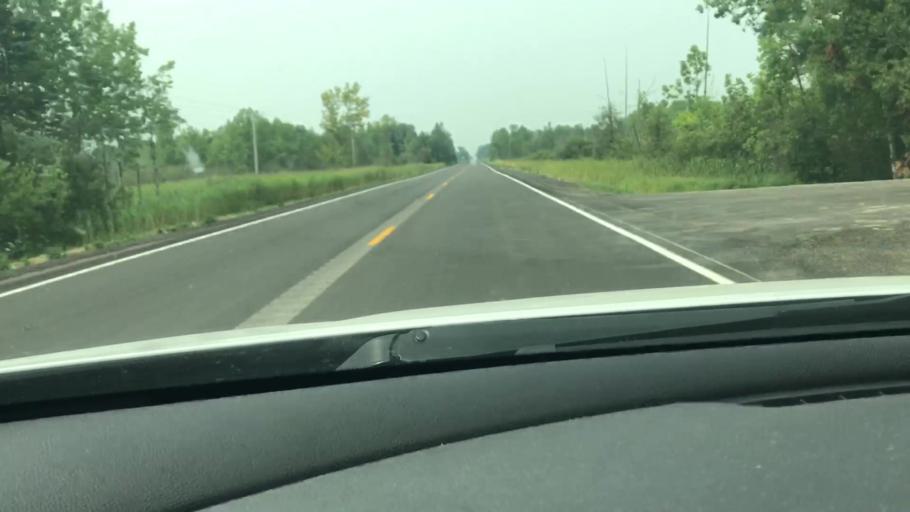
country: US
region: Minnesota
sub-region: Itasca County
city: Cohasset
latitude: 47.3517
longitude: -93.8411
